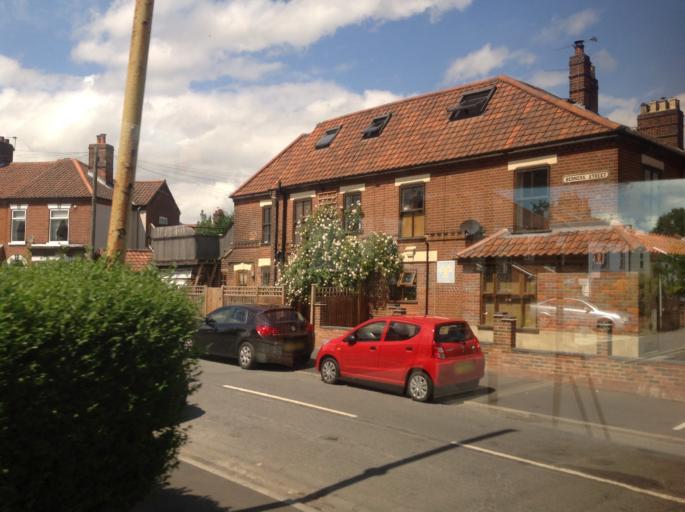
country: GB
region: England
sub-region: Norfolk
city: Norwich
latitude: 52.6454
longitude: 1.2841
